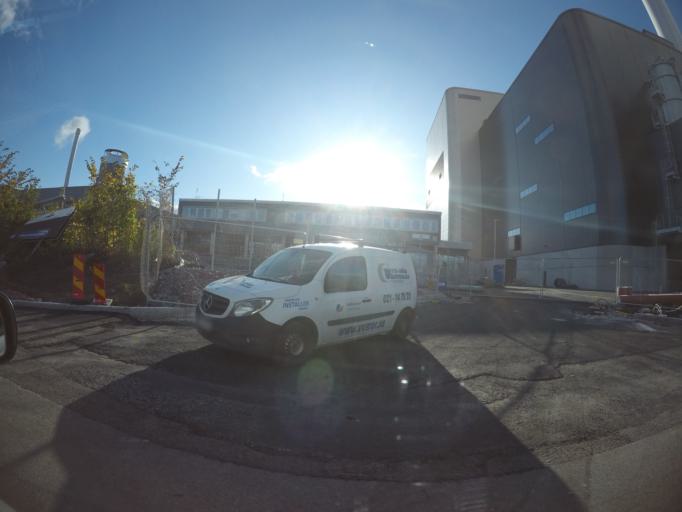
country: SE
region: Vaestmanland
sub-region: Vasteras
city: Vasteras
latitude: 59.5895
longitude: 16.5078
